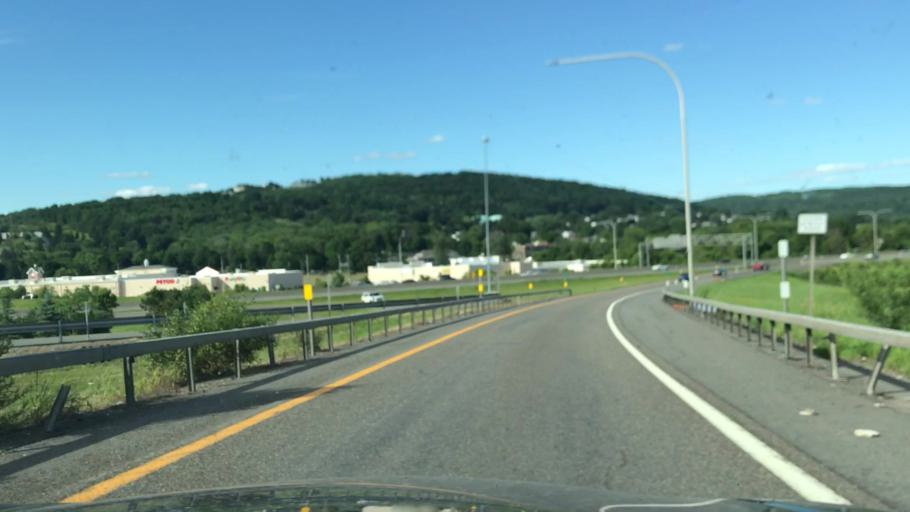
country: US
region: New York
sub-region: Broome County
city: Johnson City
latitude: 42.1182
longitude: -75.9675
